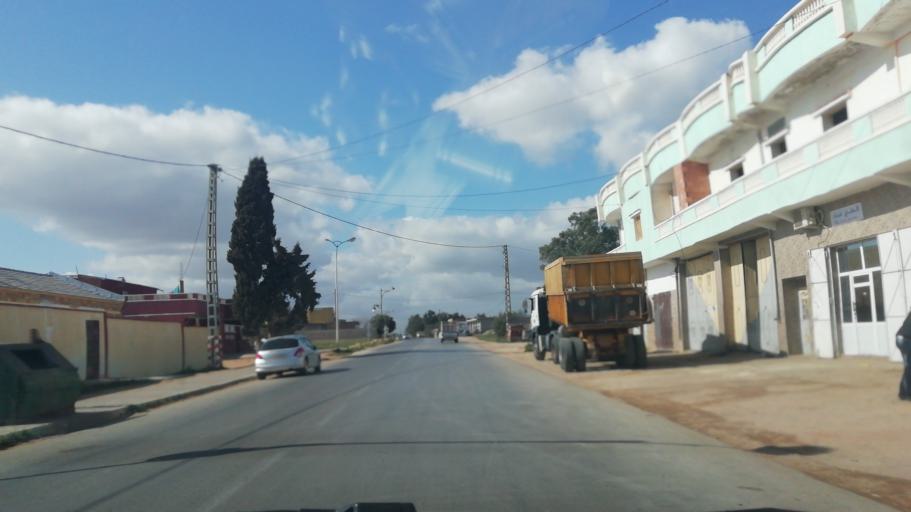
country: DZ
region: Relizane
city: Mazouna
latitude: 36.2682
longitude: 0.6279
